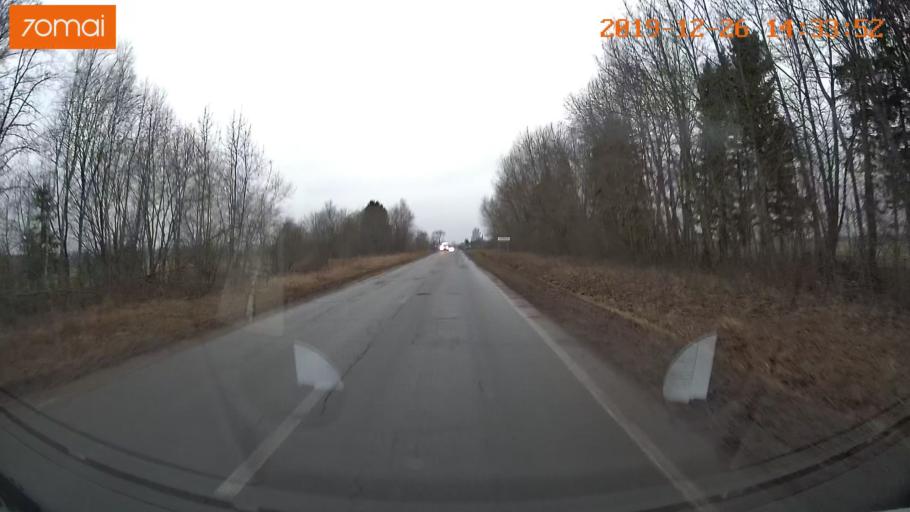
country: RU
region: Jaroslavl
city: Poshekhon'ye
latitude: 58.4288
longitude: 39.0088
